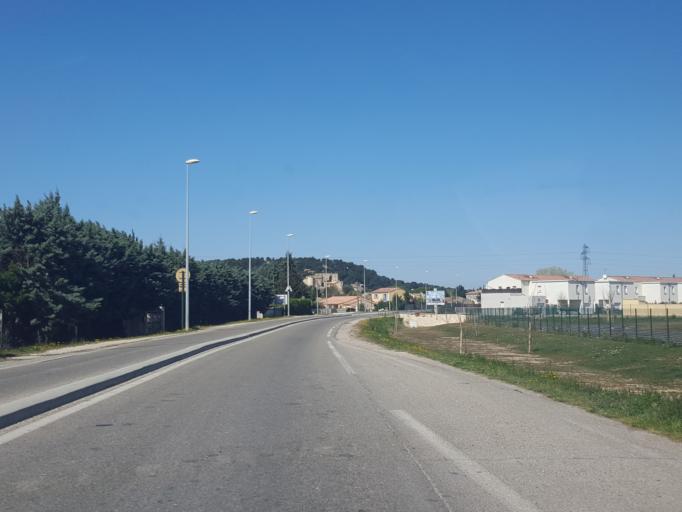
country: FR
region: Provence-Alpes-Cote d'Azur
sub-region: Departement du Vaucluse
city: Vedene
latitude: 43.9739
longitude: 4.9117
